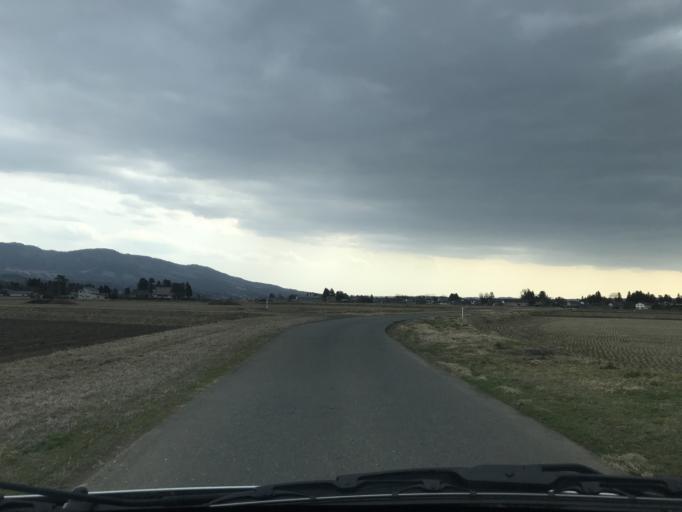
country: JP
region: Iwate
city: Mizusawa
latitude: 39.0740
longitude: 141.1553
